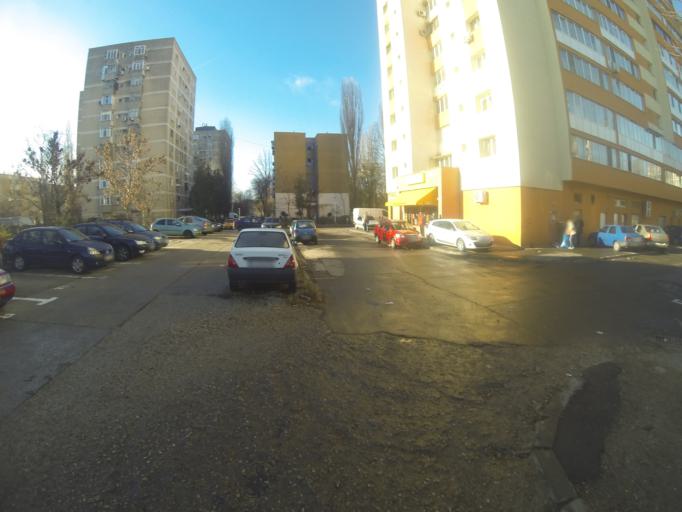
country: RO
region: Bucuresti
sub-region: Municipiul Bucuresti
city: Bucuresti
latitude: 44.4075
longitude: 26.0728
